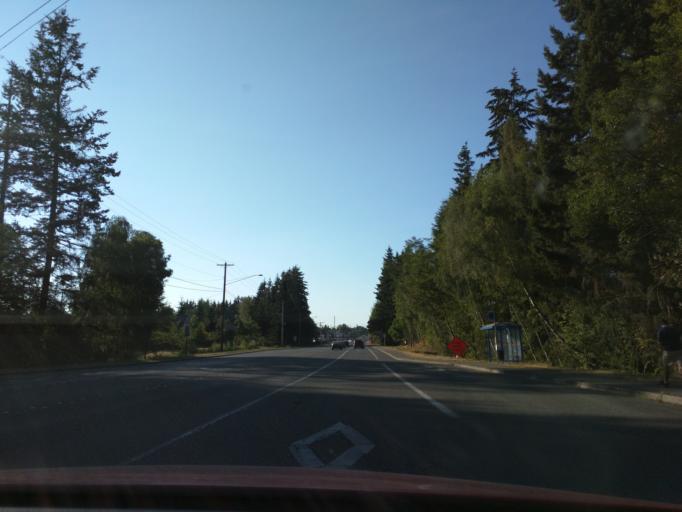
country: US
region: Washington
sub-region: Snohomish County
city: Martha Lake
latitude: 47.8845
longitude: -122.2542
